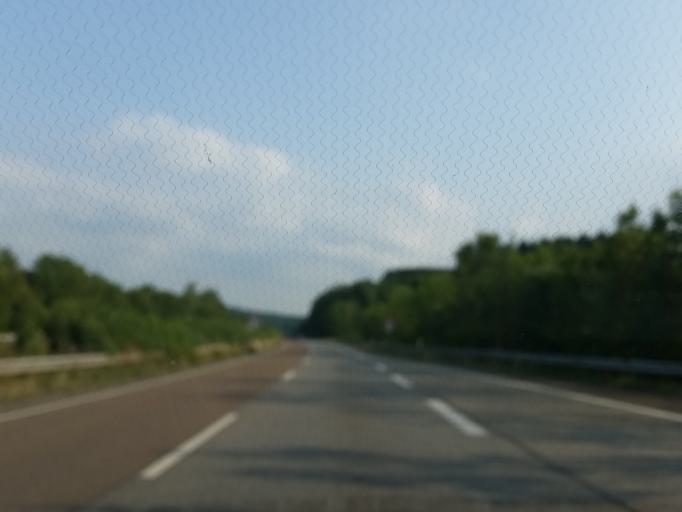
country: DE
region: Rheinland-Pfalz
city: Hermeskeil
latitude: 49.6576
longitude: 6.9230
